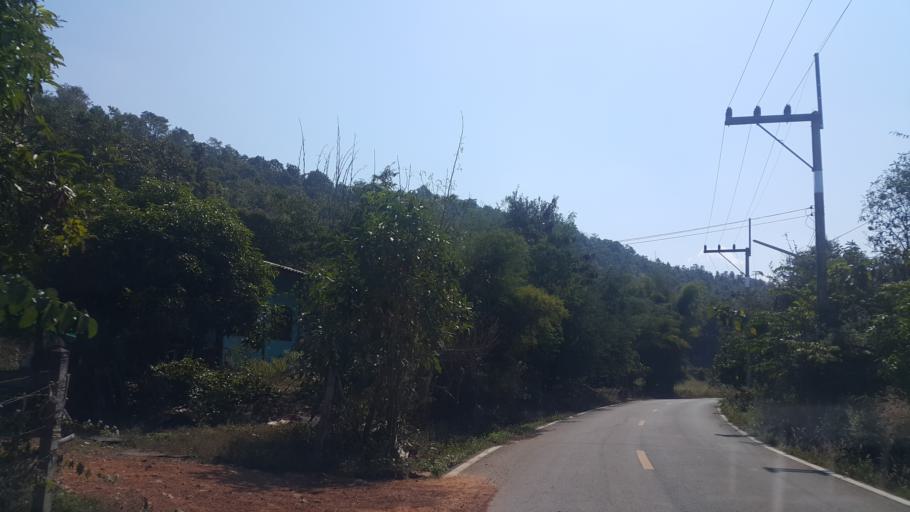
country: TH
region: Chiang Mai
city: San Kamphaeng
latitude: 18.6902
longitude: 99.1692
